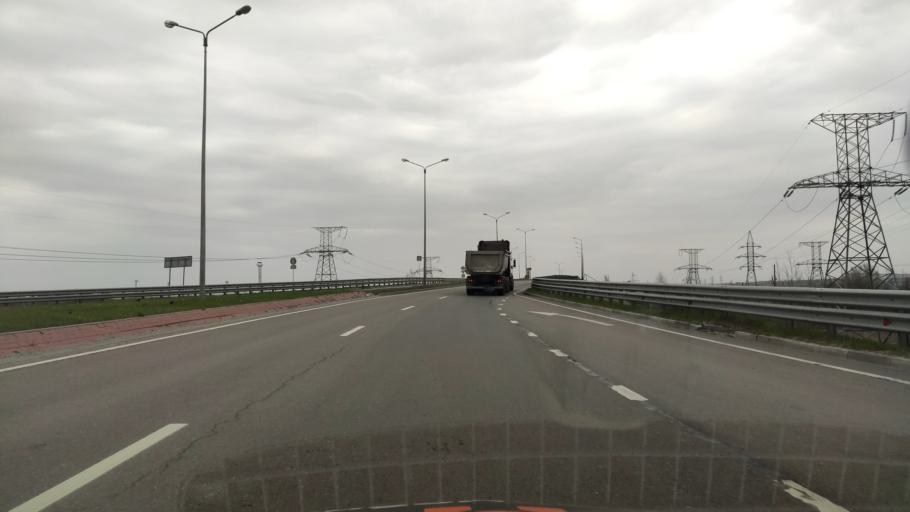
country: RU
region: Belgorod
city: Staryy Oskol
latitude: 51.3010
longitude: 37.7683
